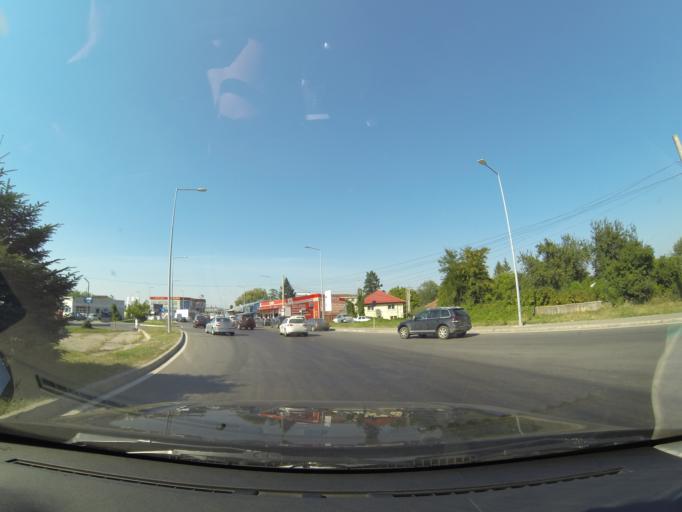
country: RO
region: Arges
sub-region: Comuna Albestii de Arges
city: Pitesti
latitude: 44.8678
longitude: 24.8841
